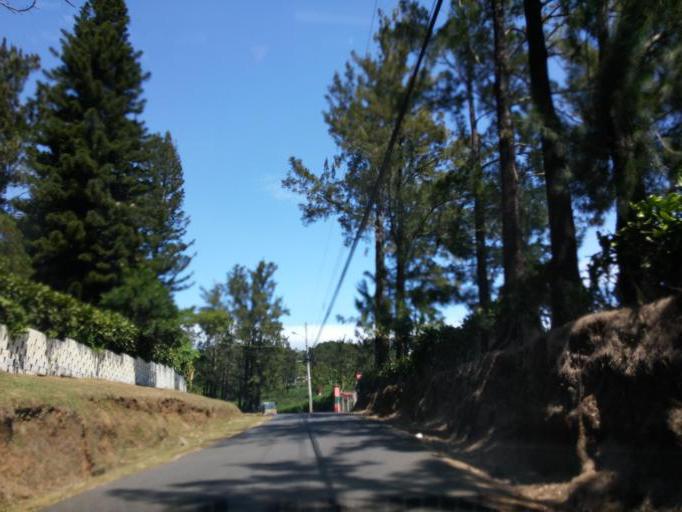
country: CR
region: Heredia
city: Santo Domingo
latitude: 10.0611
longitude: -84.1337
